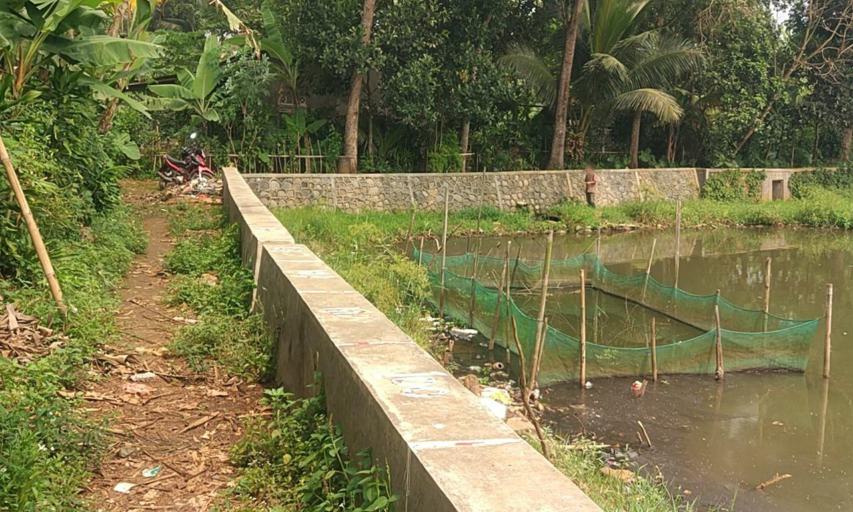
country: ID
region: West Java
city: Ciampea
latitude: -6.5335
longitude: 106.7294
